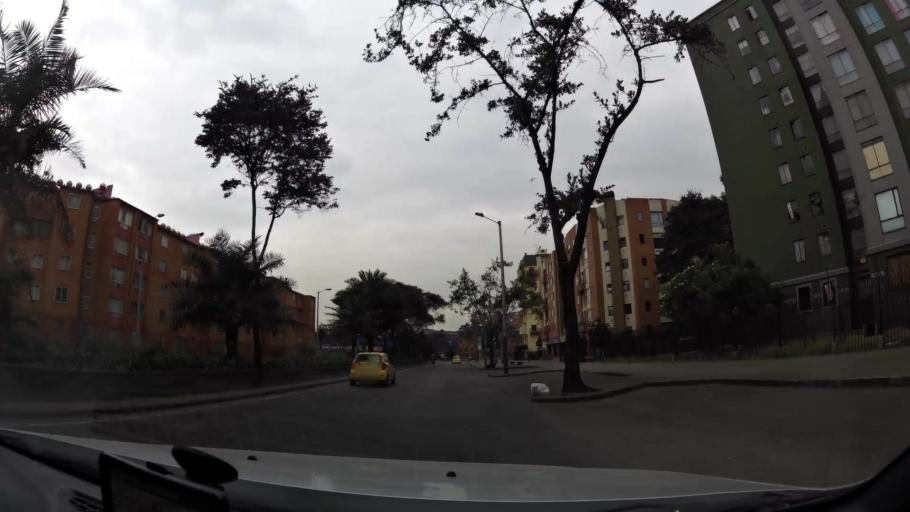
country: CO
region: Bogota D.C.
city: Bogota
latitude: 4.6576
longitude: -74.1118
